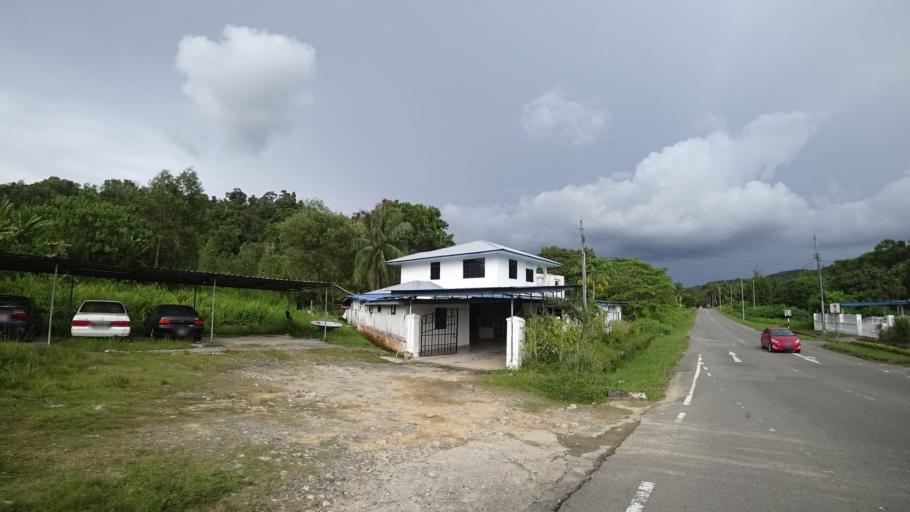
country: BN
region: Brunei and Muara
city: Bandar Seri Begawan
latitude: 4.8718
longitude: 114.9392
